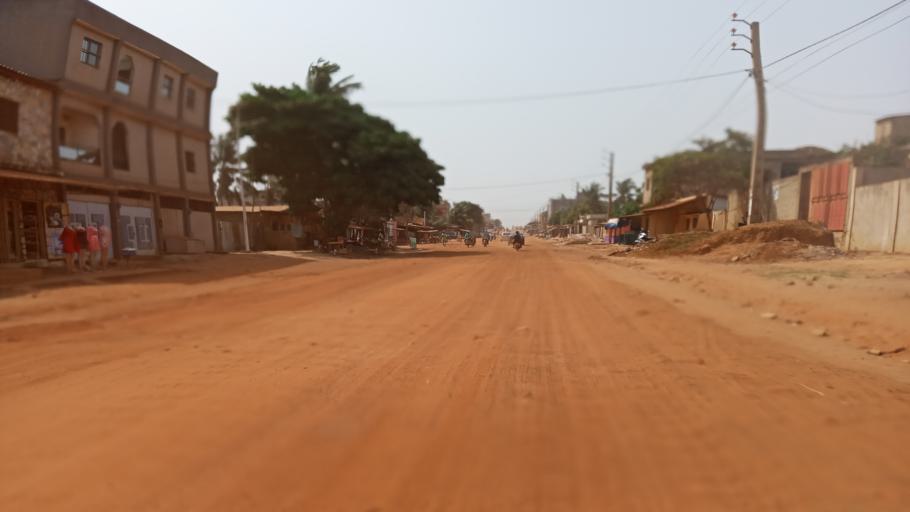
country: TG
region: Maritime
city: Lome
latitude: 6.1995
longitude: 1.1705
